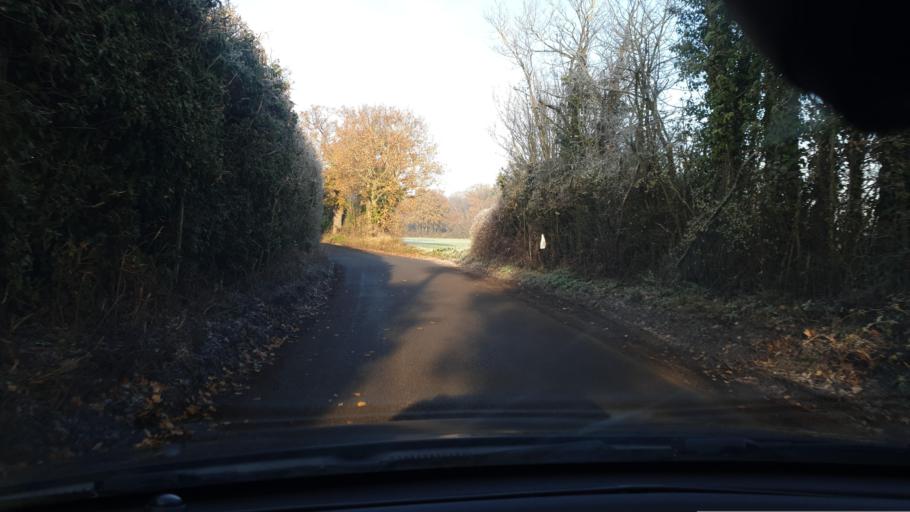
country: GB
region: England
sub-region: Essex
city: Mistley
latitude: 51.9729
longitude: 1.1227
